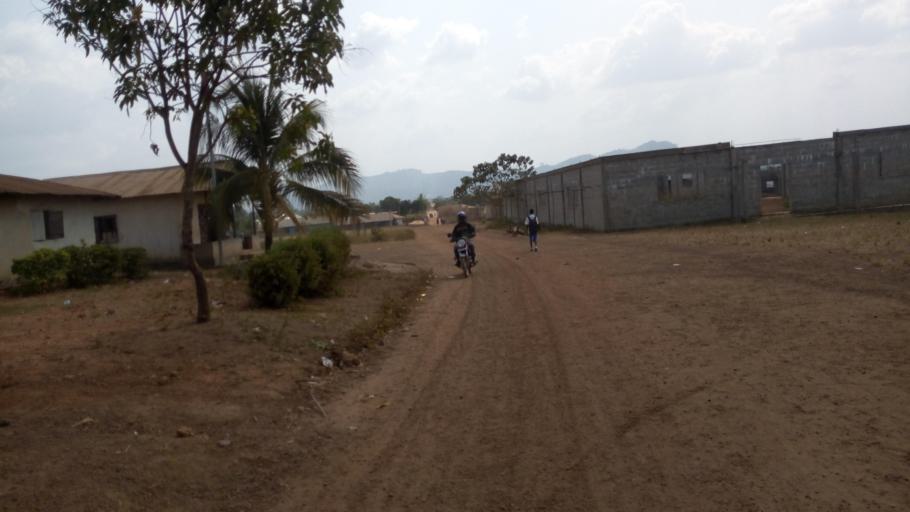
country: SL
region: Southern Province
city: Mogbwemo
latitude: 7.7798
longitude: -12.3005
